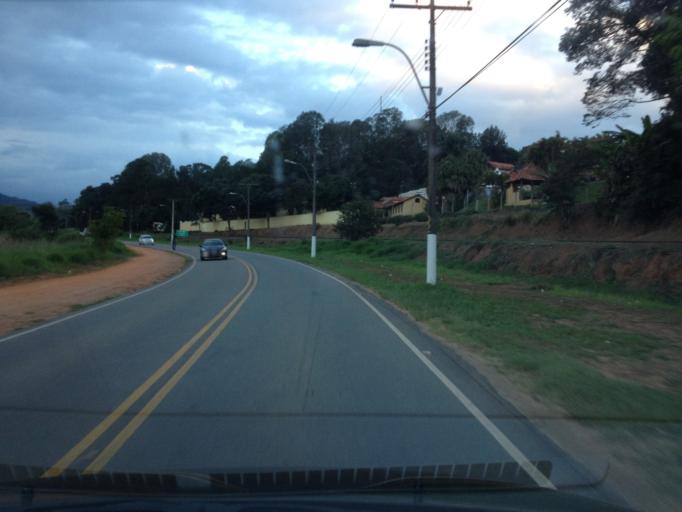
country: BR
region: Minas Gerais
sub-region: Sao Lourenco
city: Sao Lourenco
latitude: -22.0958
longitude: -45.0464
